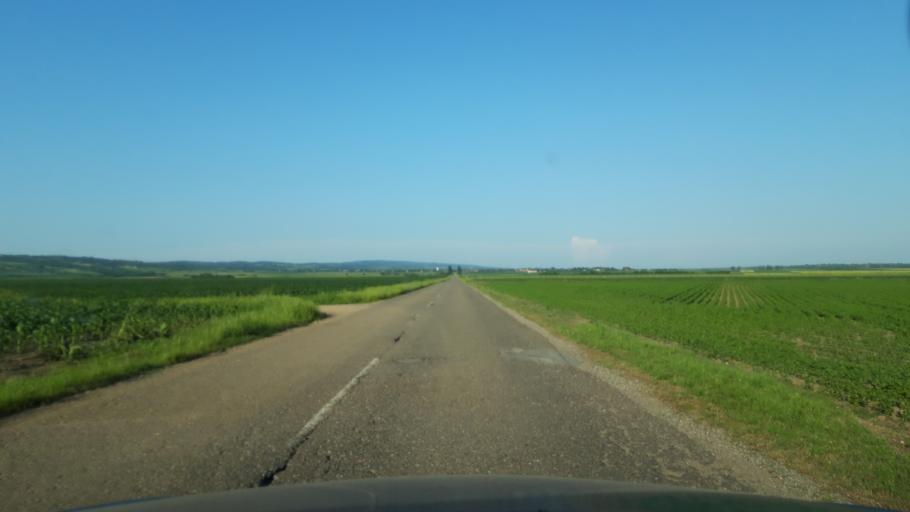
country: HR
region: Vukovarsko-Srijemska
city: Ilok
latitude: 45.1021
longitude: 19.4617
